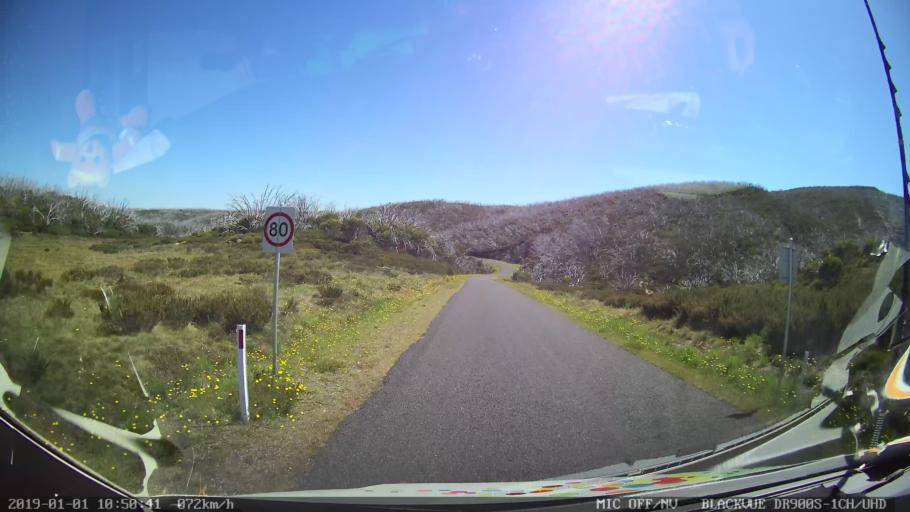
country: AU
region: New South Wales
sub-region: Snowy River
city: Jindabyne
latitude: -36.0261
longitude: 148.3714
